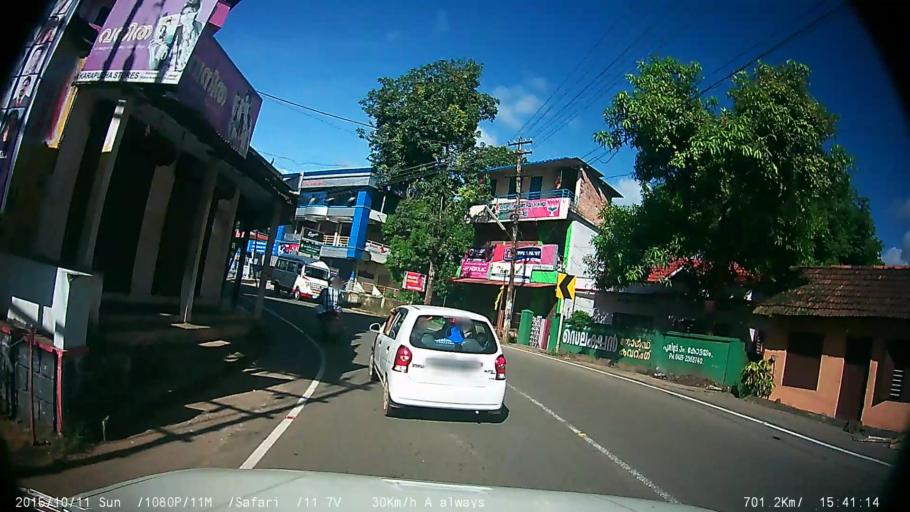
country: IN
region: Kerala
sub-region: Kottayam
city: Kottayam
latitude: 9.5575
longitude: 76.5717
